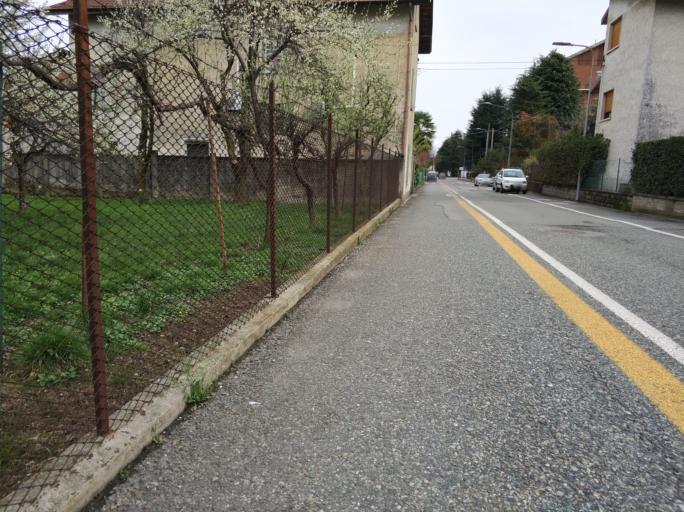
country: IT
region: Piedmont
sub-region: Provincia di Torino
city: Cirie
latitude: 45.2299
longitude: 7.5997
